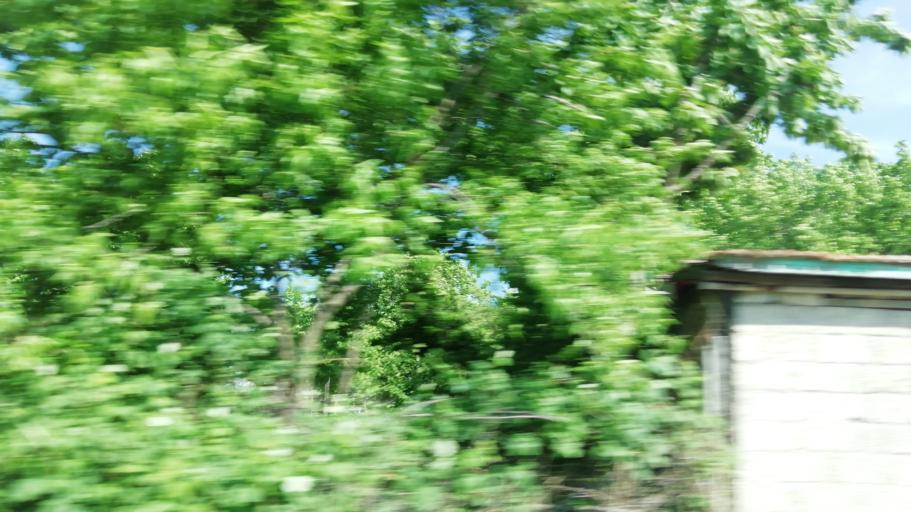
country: TR
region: Karabuk
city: Karabuk
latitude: 41.0965
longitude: 32.5928
